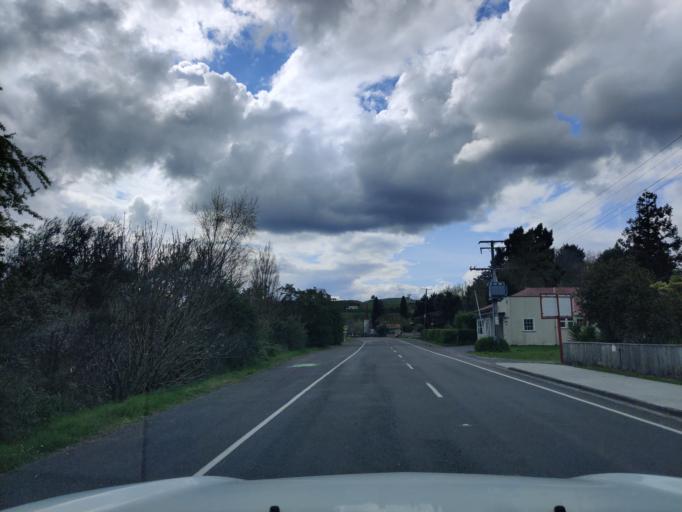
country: NZ
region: Manawatu-Wanganui
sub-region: Wanganui District
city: Wanganui
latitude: -39.8681
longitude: 175.1141
